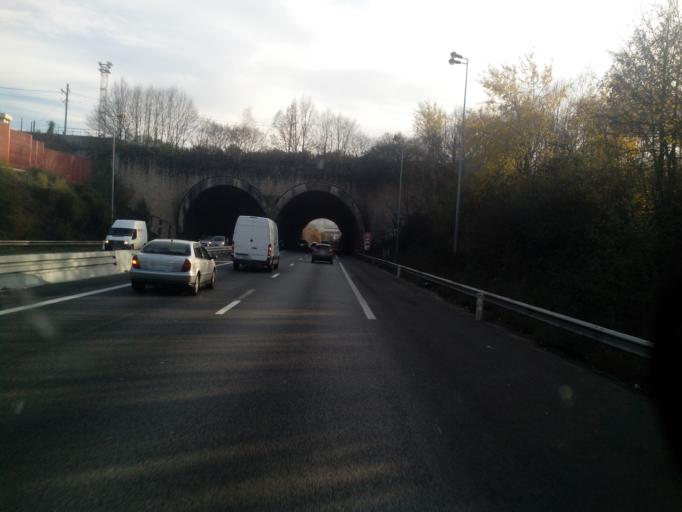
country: FR
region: Limousin
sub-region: Departement de la Haute-Vienne
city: Limoges
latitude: 45.8447
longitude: 1.2778
